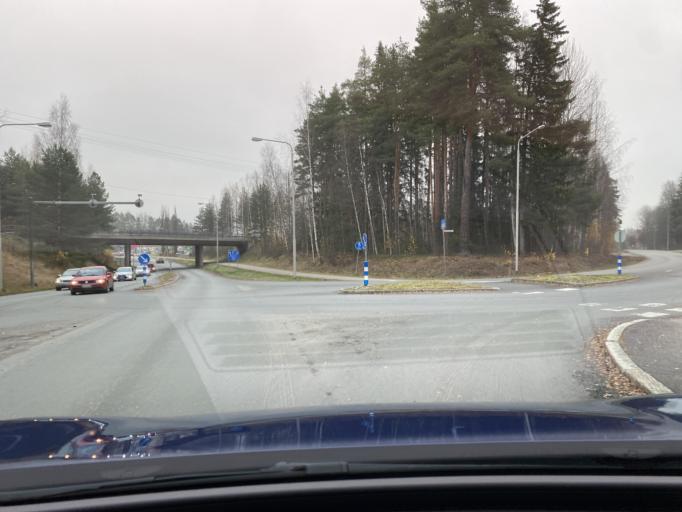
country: FI
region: Pirkanmaa
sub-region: Tampere
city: Nokia
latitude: 61.4628
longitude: 23.5045
